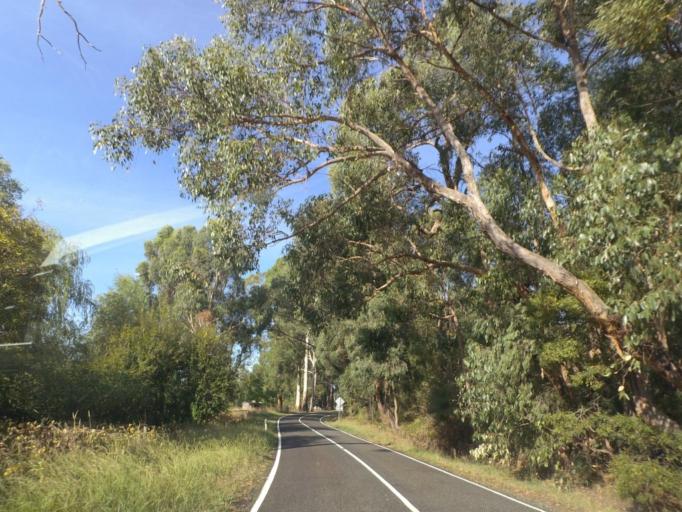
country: AU
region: Victoria
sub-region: Yarra Ranges
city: Macclesfield
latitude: -37.8147
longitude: 145.4533
